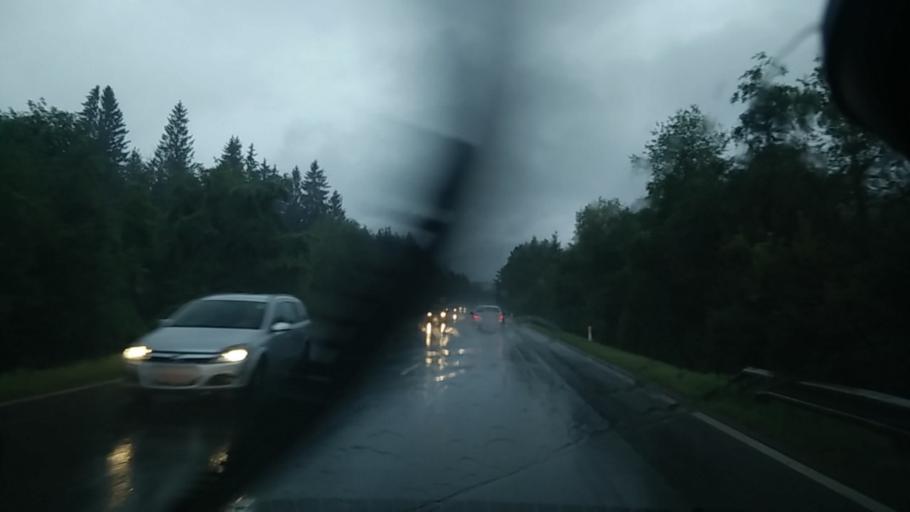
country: AT
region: Carinthia
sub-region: Villach Stadt
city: Villach
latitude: 46.5849
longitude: 13.8342
